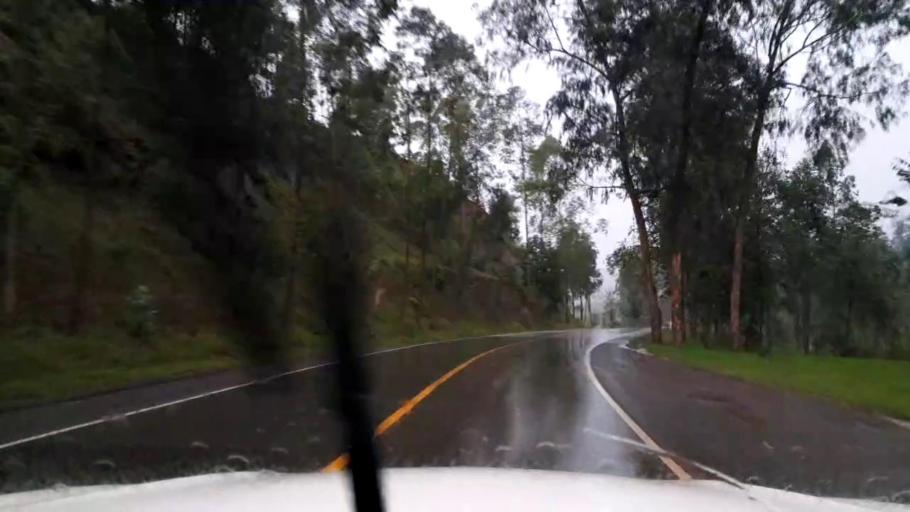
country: RW
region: Northern Province
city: Musanze
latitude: -1.5362
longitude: 29.6710
